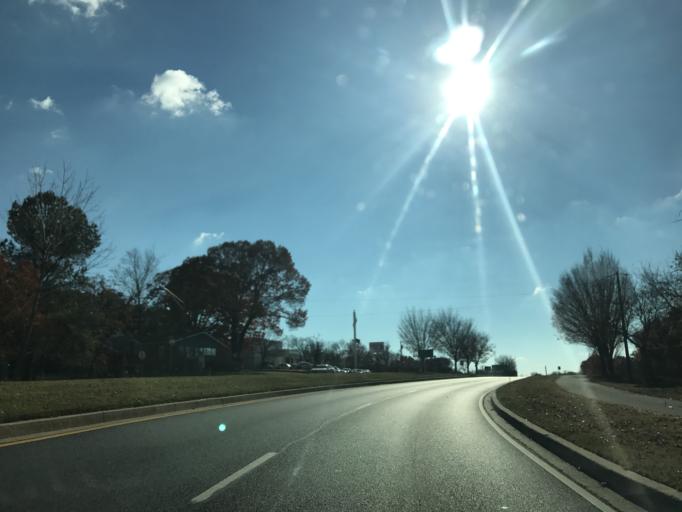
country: US
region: Maryland
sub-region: Anne Arundel County
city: Ferndale
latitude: 39.1896
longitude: -76.6535
